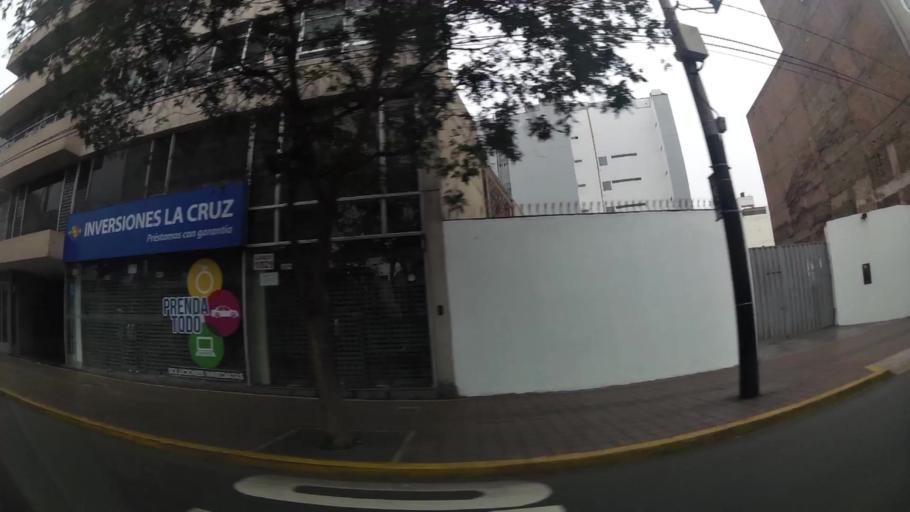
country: PE
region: Lima
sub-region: Lima
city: San Isidro
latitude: -12.1281
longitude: -77.0296
